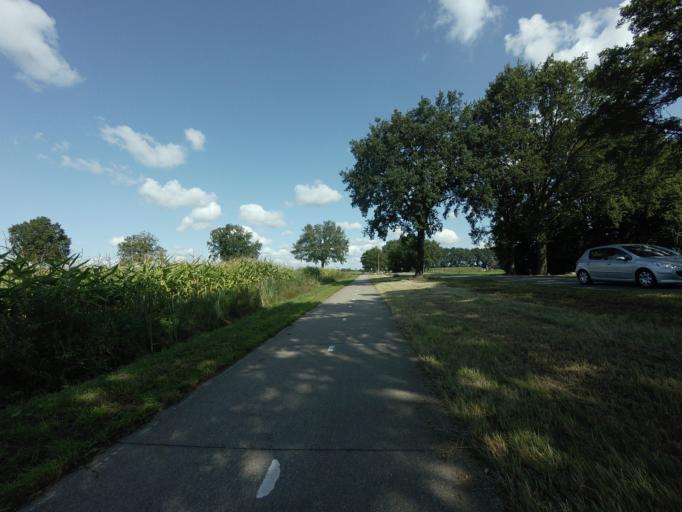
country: NL
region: Overijssel
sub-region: Gemeente Dalfsen
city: Dalfsen
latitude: 52.5482
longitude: 6.2617
